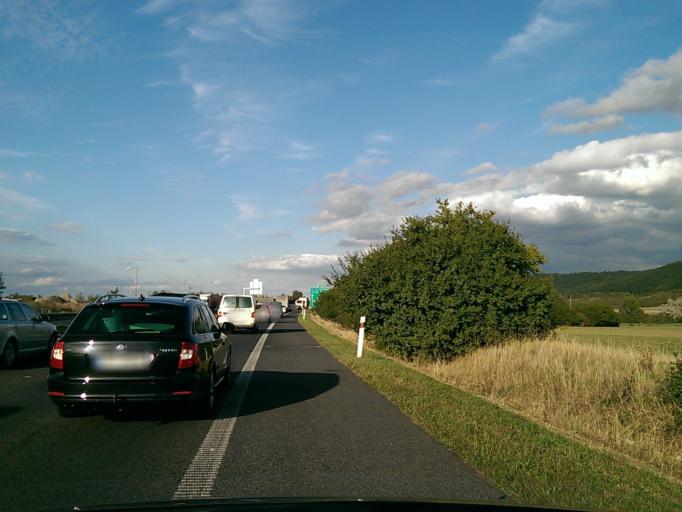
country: CZ
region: Central Bohemia
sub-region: Okres Mlada Boleslav
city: Mlada Boleslav
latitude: 50.3801
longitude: 14.8915
